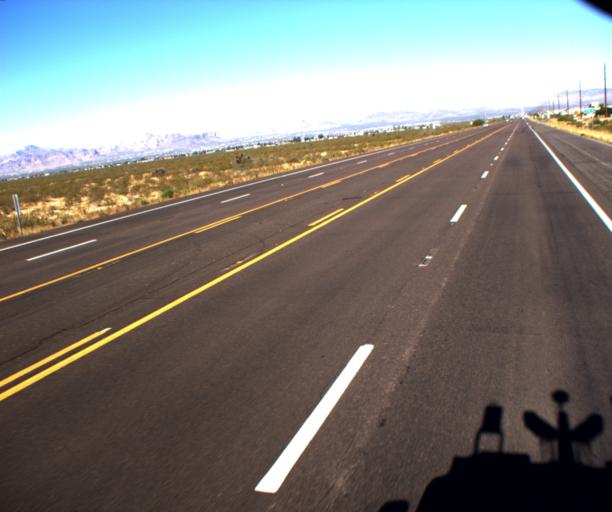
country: US
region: Arizona
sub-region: Mohave County
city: Golden Valley
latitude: 35.2212
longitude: -114.1971
